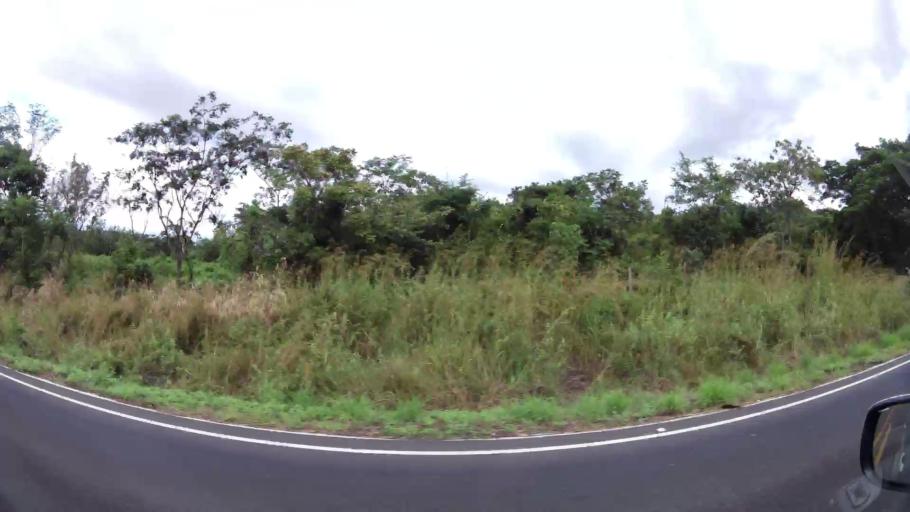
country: CR
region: Guanacaste
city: Nandayure
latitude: 10.2469
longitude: -85.2256
